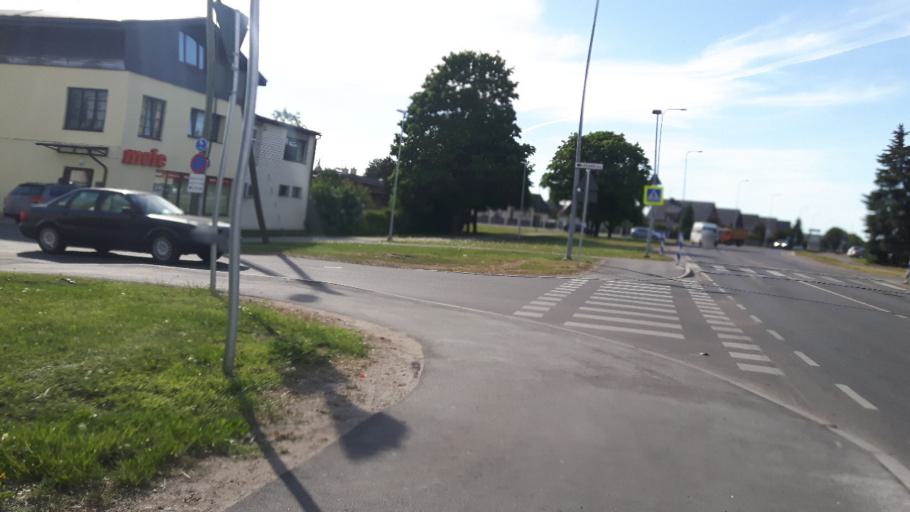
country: EE
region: Harju
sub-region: Joelaehtme vald
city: Loo
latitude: 59.4354
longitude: 24.9432
